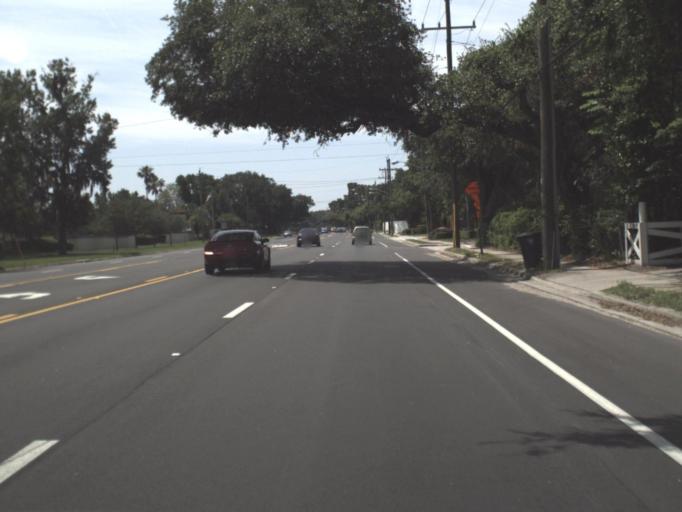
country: US
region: Florida
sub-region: Duval County
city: Jacksonville
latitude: 30.2308
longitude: -81.6171
